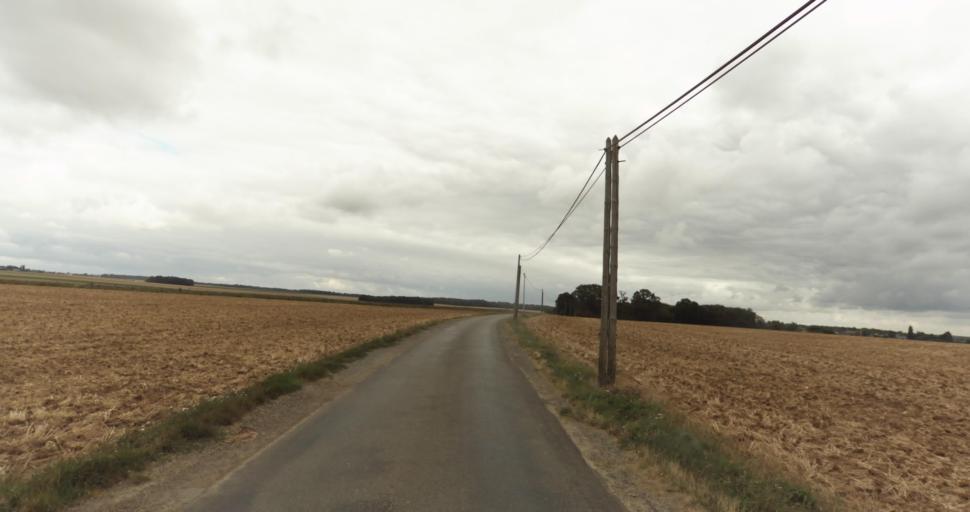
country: FR
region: Haute-Normandie
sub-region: Departement de l'Eure
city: Menilles
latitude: 49.0139
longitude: 1.3008
